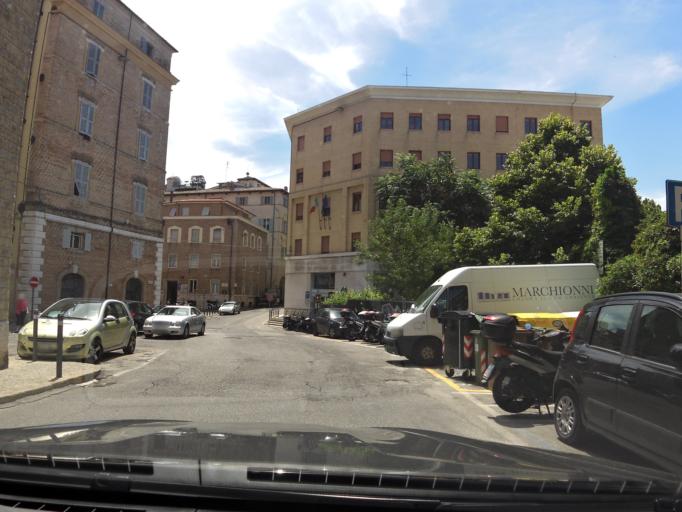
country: IT
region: The Marches
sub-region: Provincia di Ancona
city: Le Grazie di Ancona
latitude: 43.6211
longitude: 13.5102
